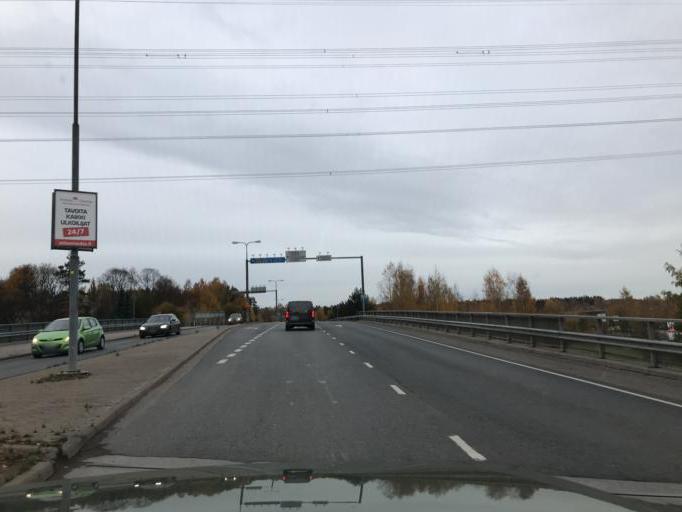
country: FI
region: Uusimaa
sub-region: Helsinki
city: Vantaa
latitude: 60.2766
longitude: 25.0785
